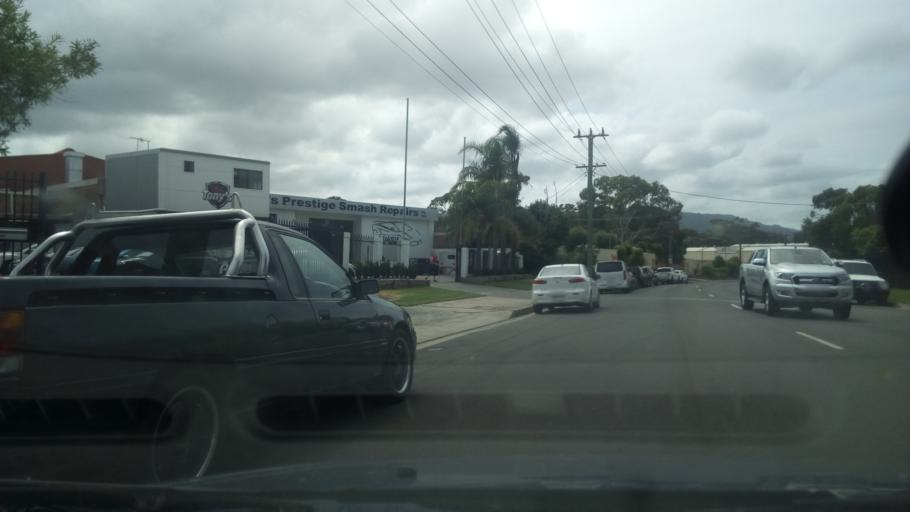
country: AU
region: New South Wales
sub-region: Wollongong
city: Fairy Meadow
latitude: -34.4074
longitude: 150.8950
